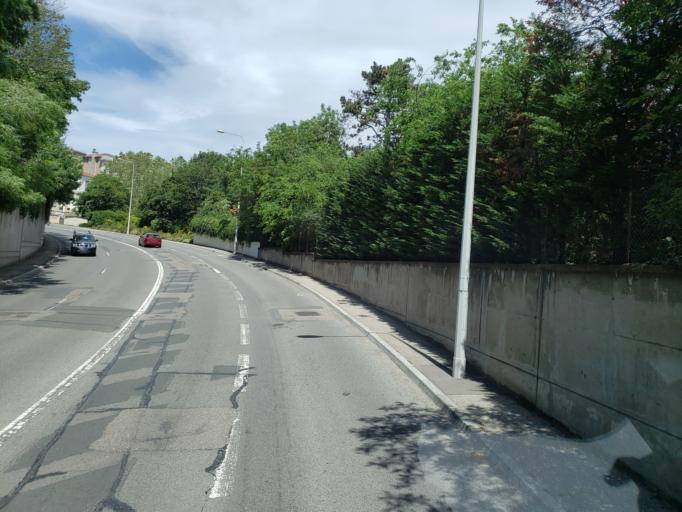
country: FR
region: Rhone-Alpes
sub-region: Departement du Rhone
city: Sainte-Foy-les-Lyon
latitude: 45.7530
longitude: 4.8142
